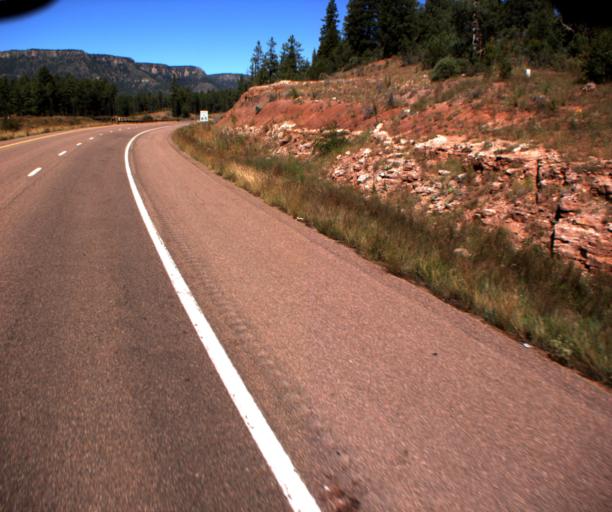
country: US
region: Arizona
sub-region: Gila County
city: Star Valley
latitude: 34.3072
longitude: -110.9959
